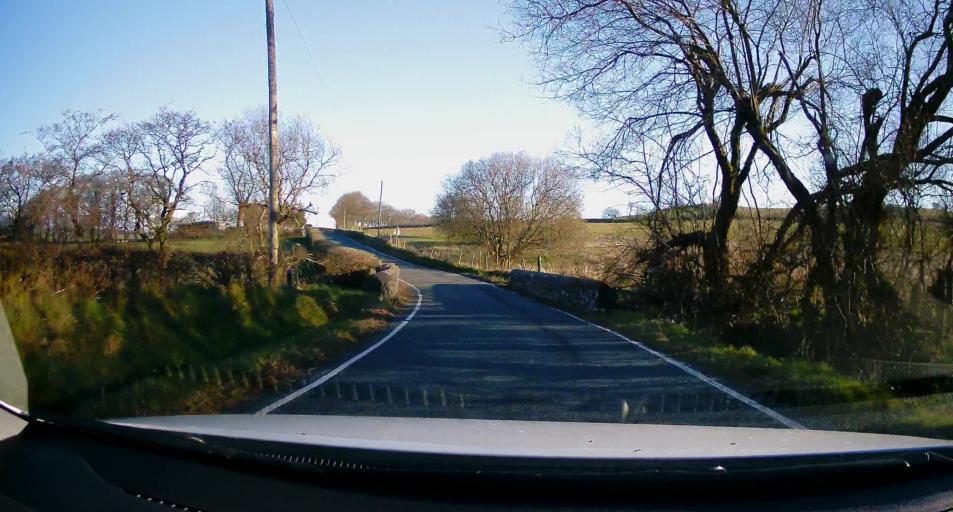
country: GB
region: Wales
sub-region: County of Ceredigion
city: Lledrod
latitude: 52.2636
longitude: -4.0716
